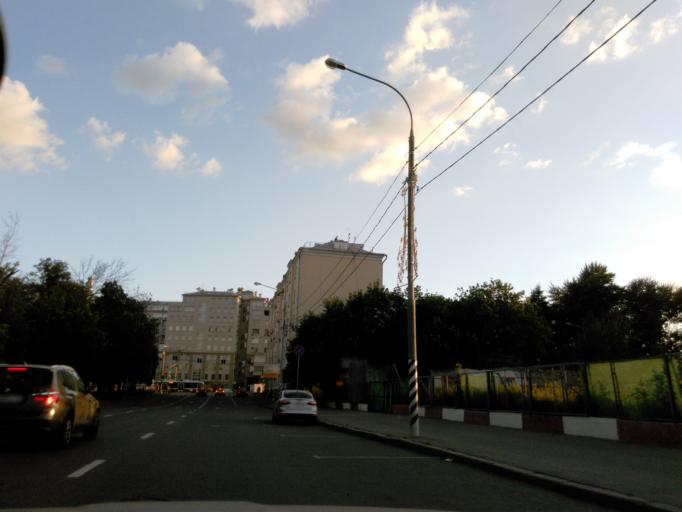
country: RU
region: Moscow
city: Moscow
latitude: 55.7455
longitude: 37.6166
